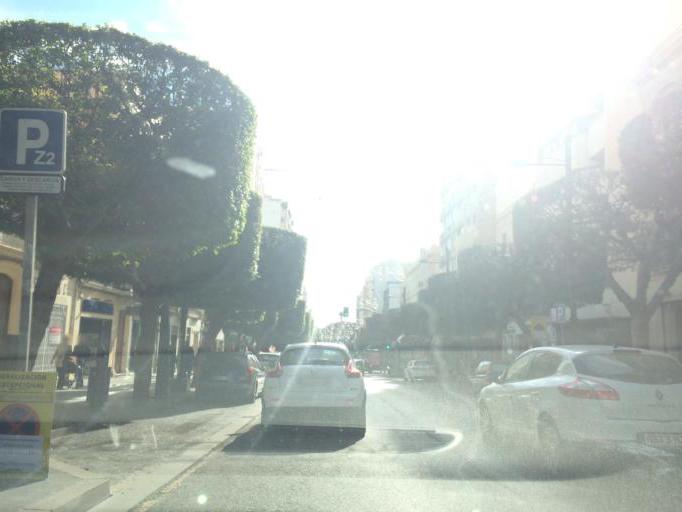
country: ES
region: Andalusia
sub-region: Provincia de Almeria
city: Almeria
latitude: 36.8402
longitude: -2.4637
